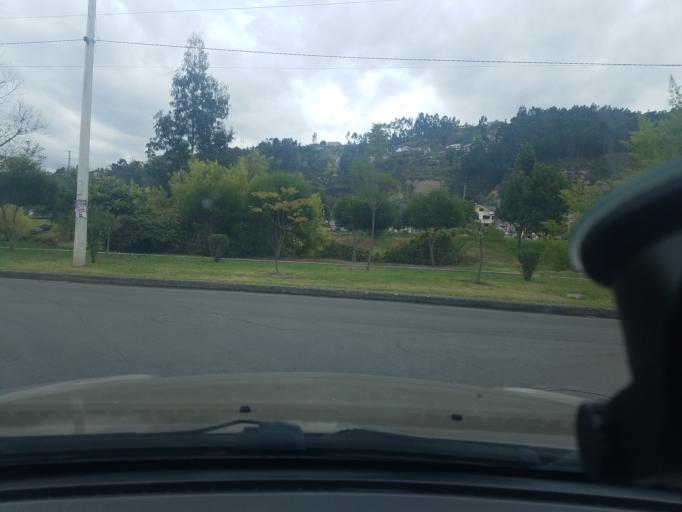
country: EC
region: Azuay
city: Cuenca
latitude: -2.9071
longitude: -78.9845
